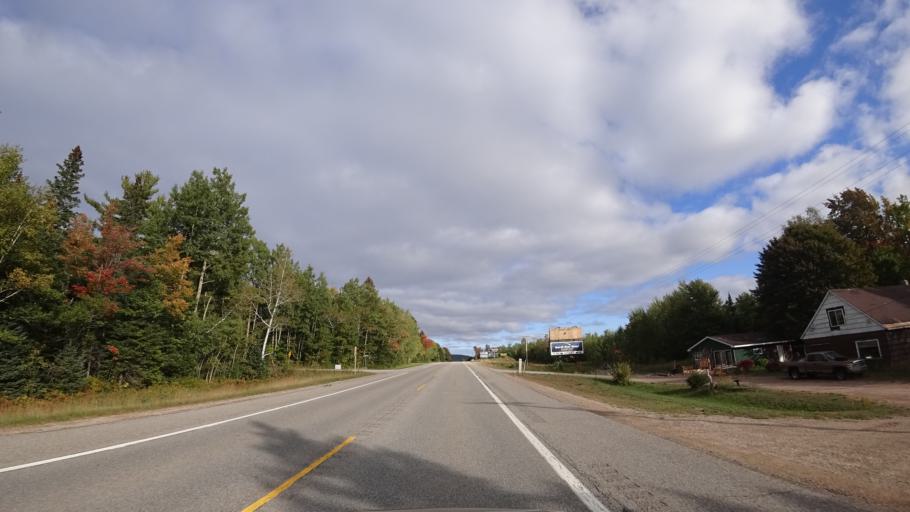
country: US
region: Michigan
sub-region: Alger County
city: Munising
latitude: 46.4406
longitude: -86.7215
